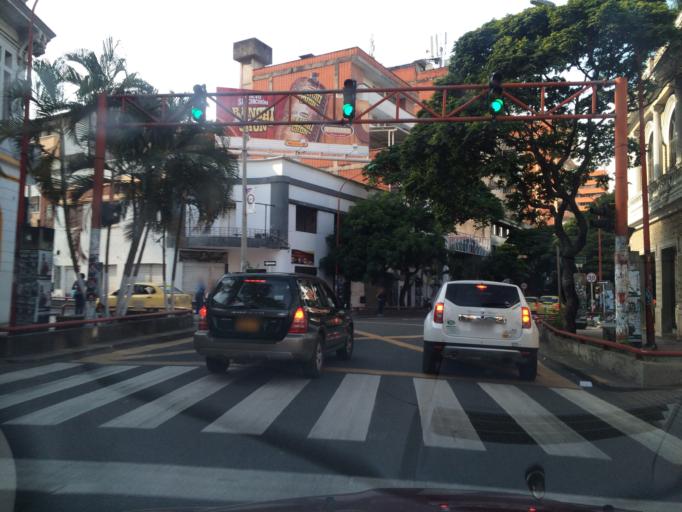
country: CO
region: Valle del Cauca
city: Cali
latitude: 3.4568
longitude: -76.5339
